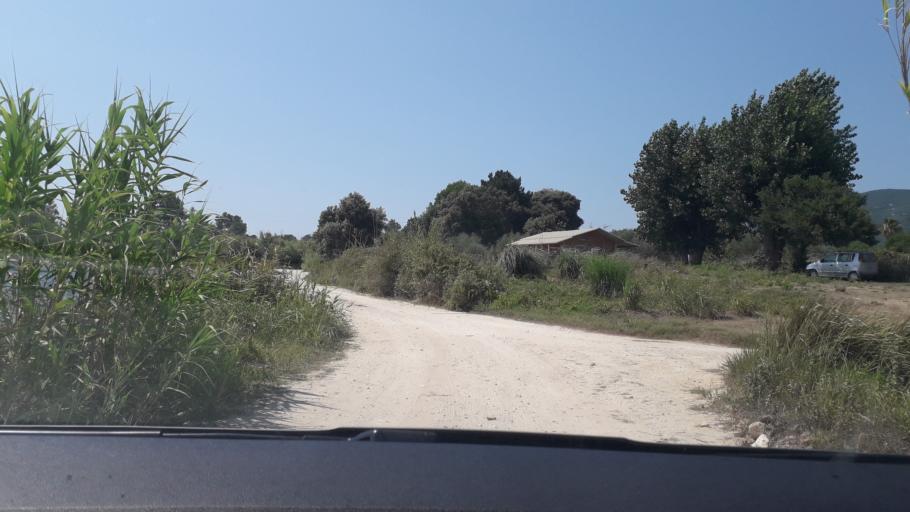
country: GR
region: Ionian Islands
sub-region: Nomos Kerkyras
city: Agios Matthaios
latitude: 39.4553
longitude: 19.8780
